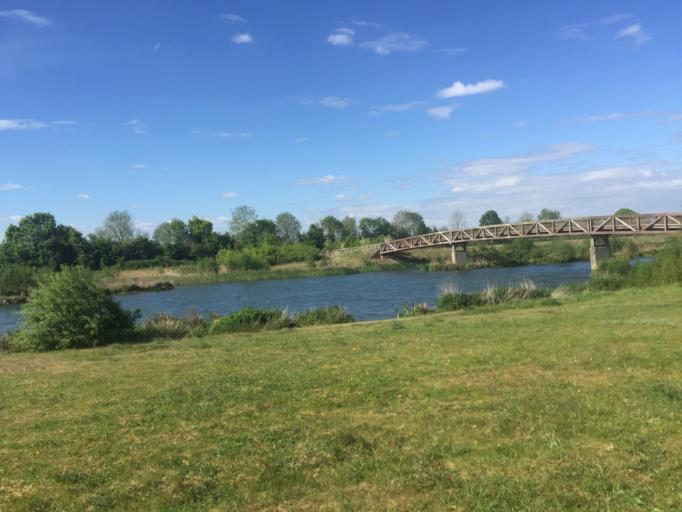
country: GB
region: England
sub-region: Royal Borough of Windsor and Maidenhead
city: Bray
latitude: 51.5059
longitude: -0.6672
